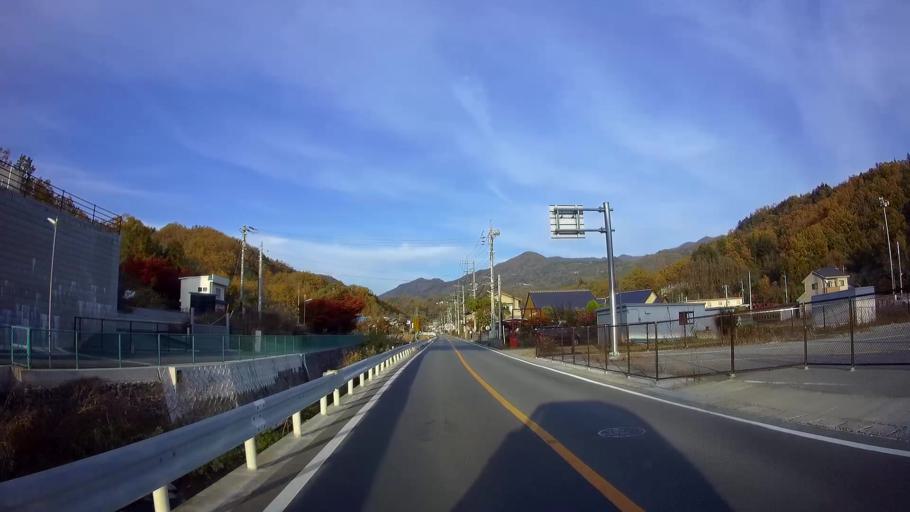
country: JP
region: Yamanashi
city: Ryuo
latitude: 35.5023
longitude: 138.4686
